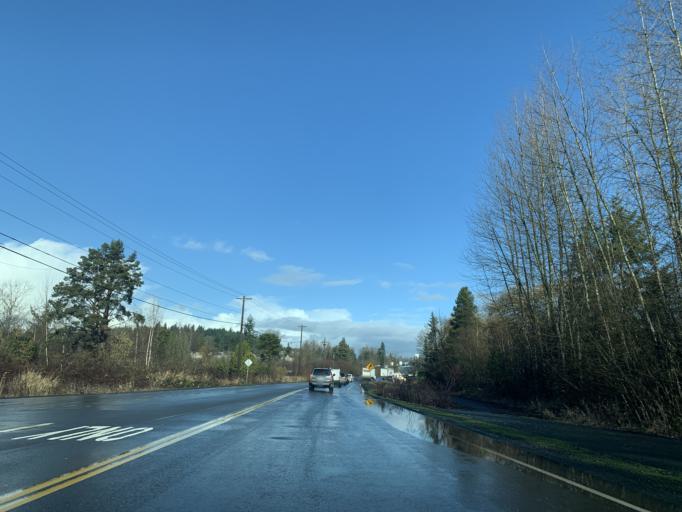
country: US
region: Washington
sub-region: Pierce County
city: Fife
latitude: 47.2398
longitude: -122.3363
